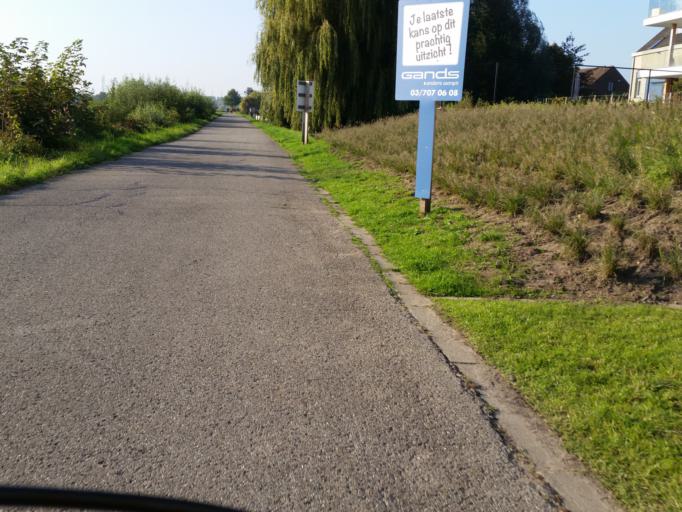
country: BE
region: Flanders
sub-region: Provincie Antwerpen
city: Niel
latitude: 51.0994
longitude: 4.3339
